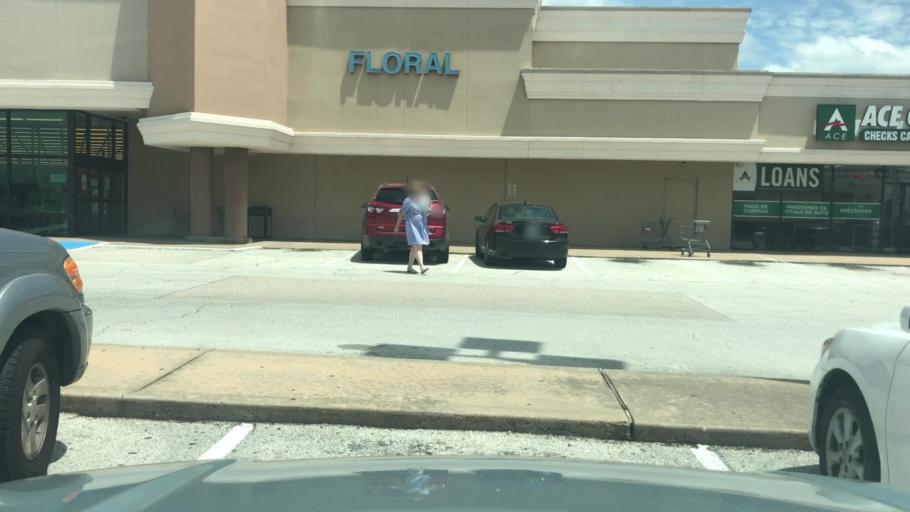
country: US
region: Texas
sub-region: Fort Bend County
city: Cinco Ranch
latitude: 29.7923
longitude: -95.7197
